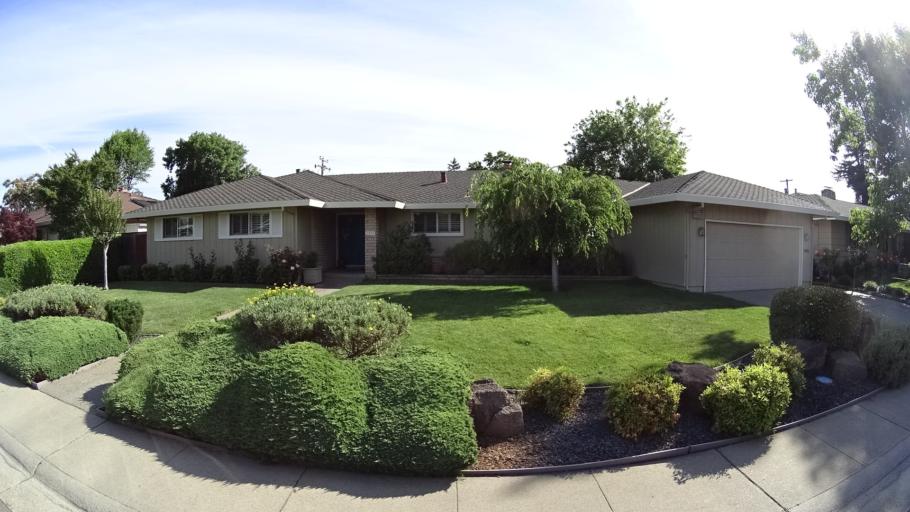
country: US
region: California
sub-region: Sacramento County
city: Rosemont
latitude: 38.5667
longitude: -121.3994
